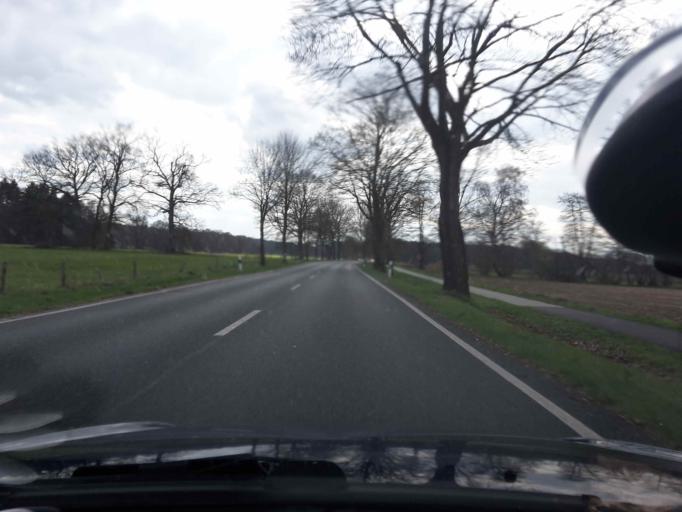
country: DE
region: Lower Saxony
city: Jesteburg
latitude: 53.3006
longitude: 9.9343
